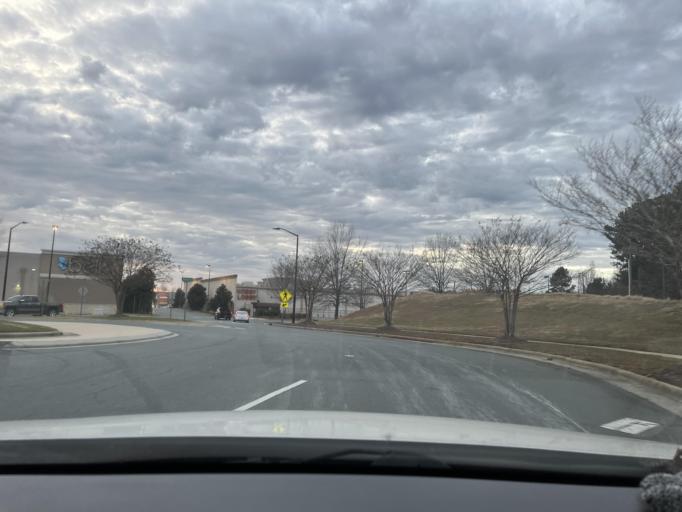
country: US
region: North Carolina
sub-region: Alamance County
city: Elon
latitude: 36.0709
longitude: -79.5049
